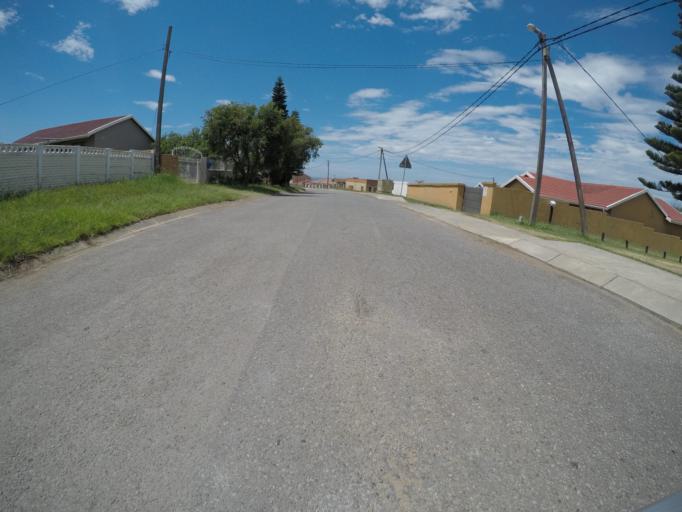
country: ZA
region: Eastern Cape
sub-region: Buffalo City Metropolitan Municipality
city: East London
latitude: -33.0427
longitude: 27.8630
